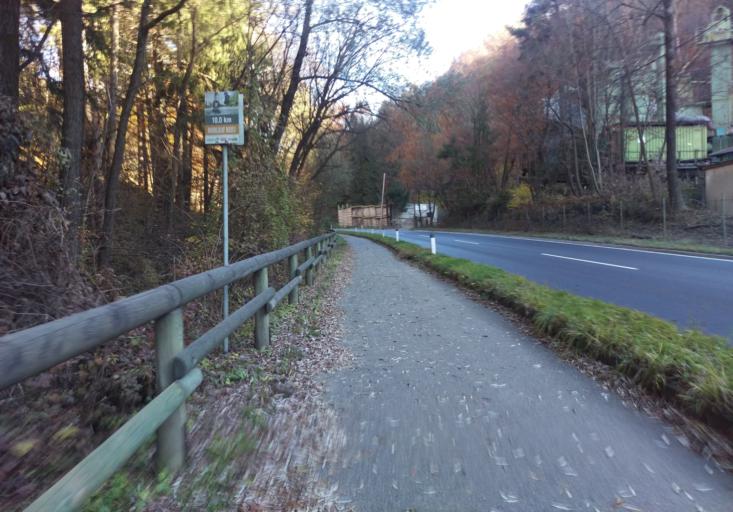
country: AT
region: Styria
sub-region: Politischer Bezirk Graz-Umgebung
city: Stattegg
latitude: 47.1329
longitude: 15.4534
